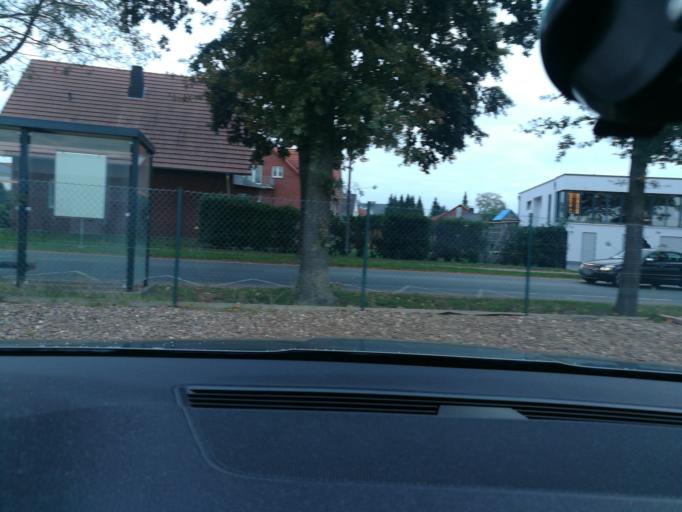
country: DE
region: North Rhine-Westphalia
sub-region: Regierungsbezirk Detmold
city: Minden
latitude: 52.3208
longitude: 8.9101
